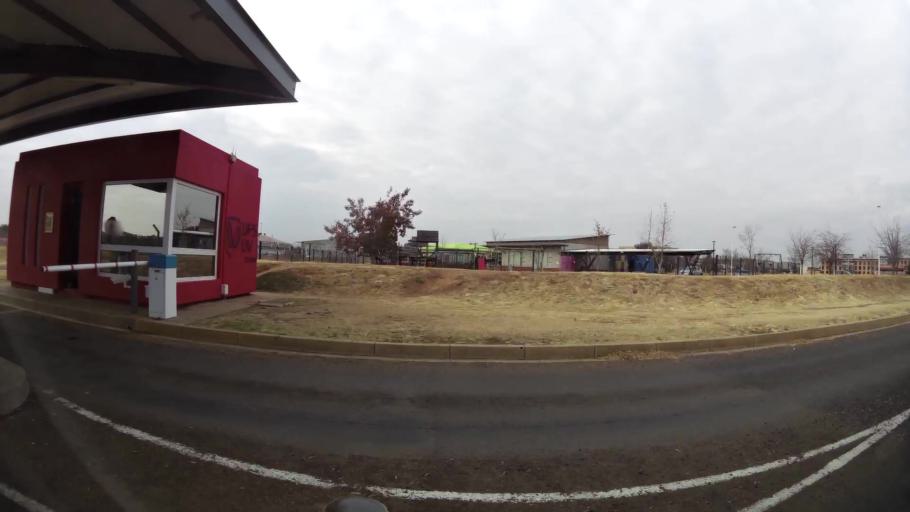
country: ZA
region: Orange Free State
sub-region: Mangaung Metropolitan Municipality
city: Bloemfontein
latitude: -29.1050
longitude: 26.1816
